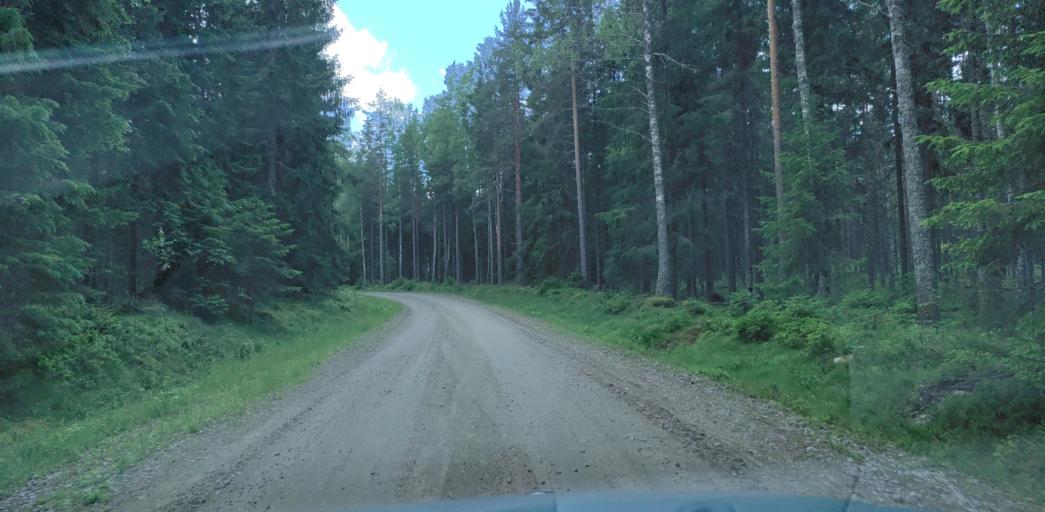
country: SE
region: Vaermland
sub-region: Hagfors Kommun
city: Ekshaerad
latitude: 60.0542
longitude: 13.3094
